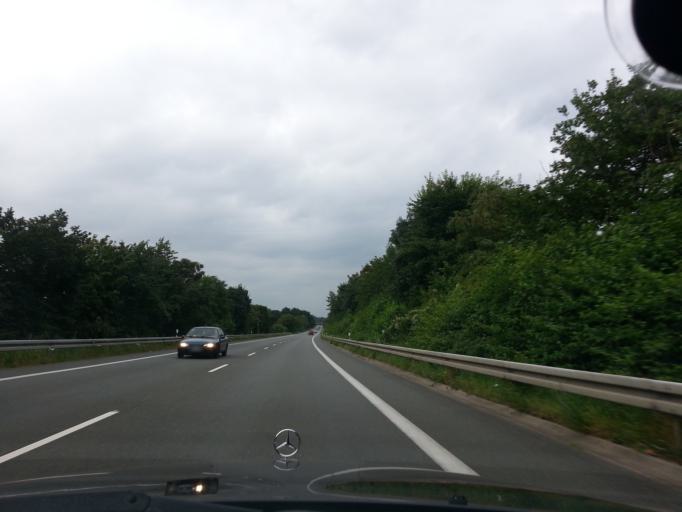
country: DE
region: North Rhine-Westphalia
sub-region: Regierungsbezirk Munster
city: Borken
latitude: 51.8448
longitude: 6.8351
